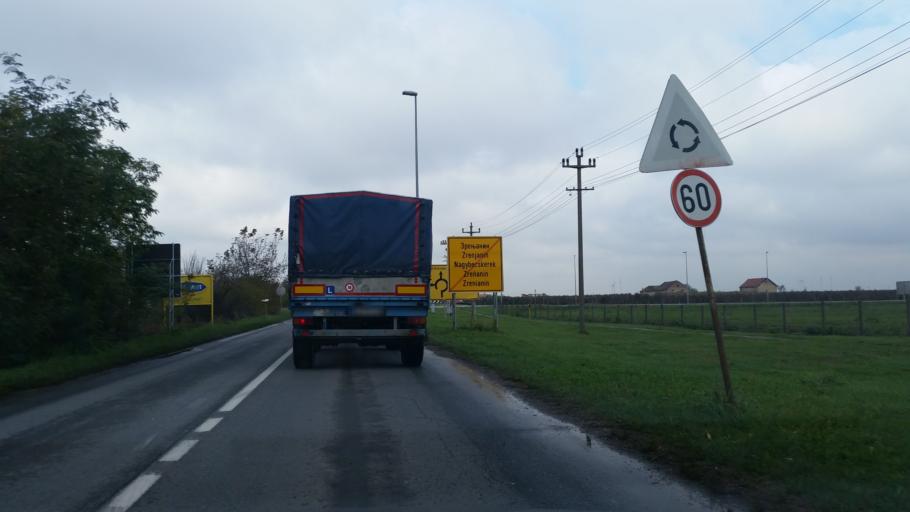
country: RS
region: Autonomna Pokrajina Vojvodina
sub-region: Srednjebanatski Okrug
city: Zrenjanin
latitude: 45.4001
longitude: 20.3771
